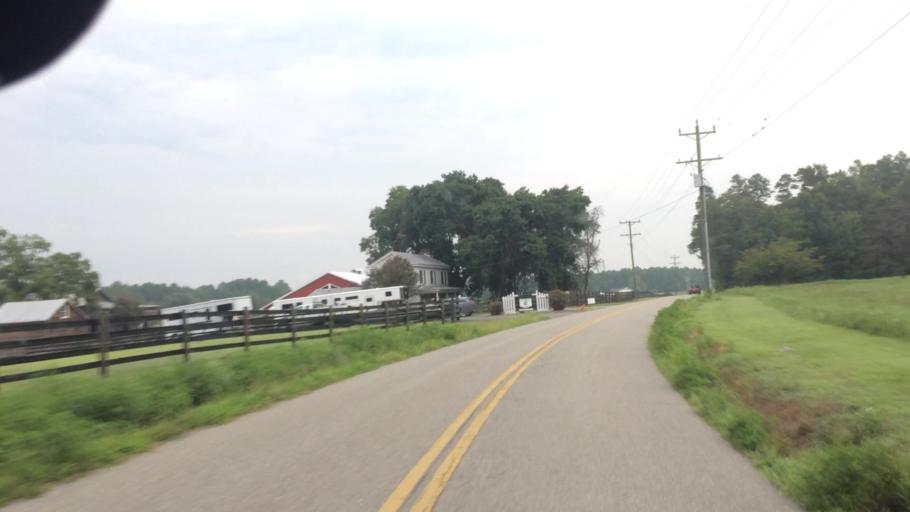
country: US
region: Virginia
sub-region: King William County
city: West Point
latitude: 37.5673
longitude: -76.7071
